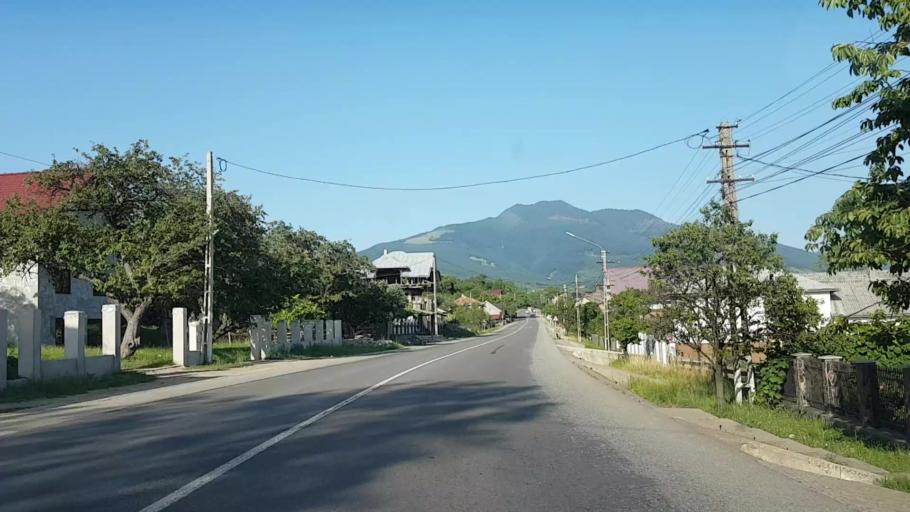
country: RO
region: Bistrita-Nasaud
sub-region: Comuna Tiha Bargaului
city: Tiha Bargaului
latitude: 47.2294
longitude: 24.7783
